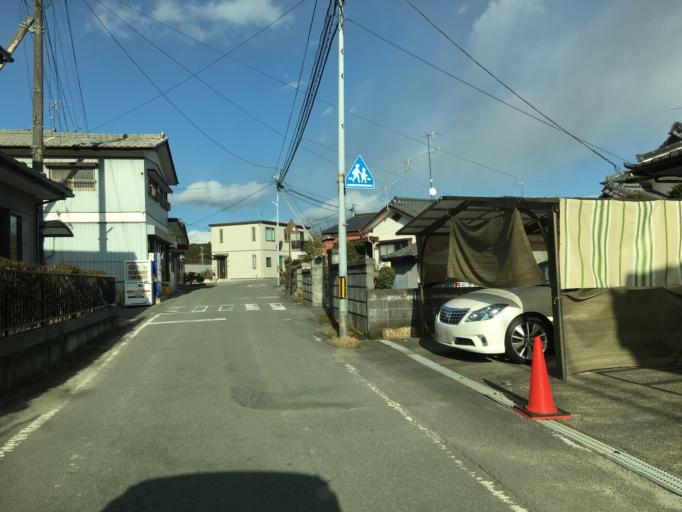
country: JP
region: Ibaraki
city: Kitaibaraki
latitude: 36.9056
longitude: 140.7322
